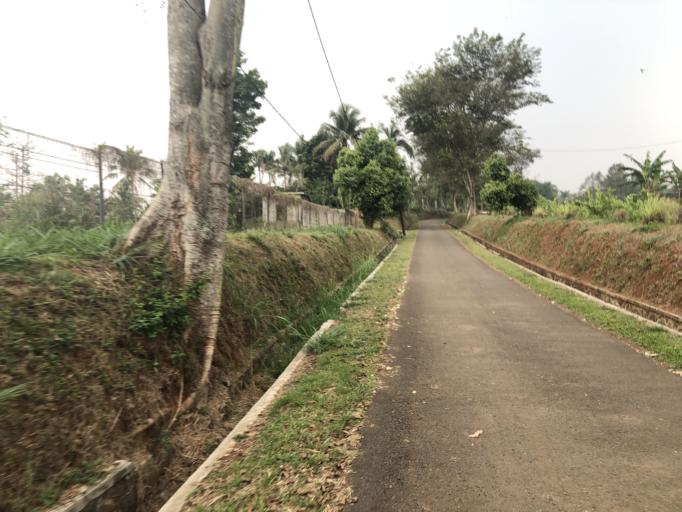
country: ID
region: West Java
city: Ciampea
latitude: -6.5519
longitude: 106.7152
